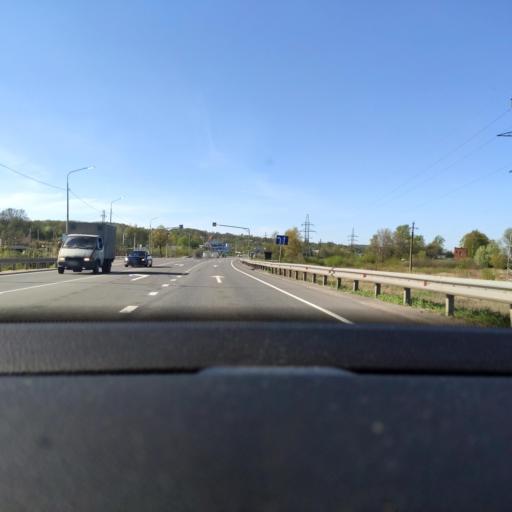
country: RU
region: Moskovskaya
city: Yakhroma
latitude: 56.3009
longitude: 37.4821
